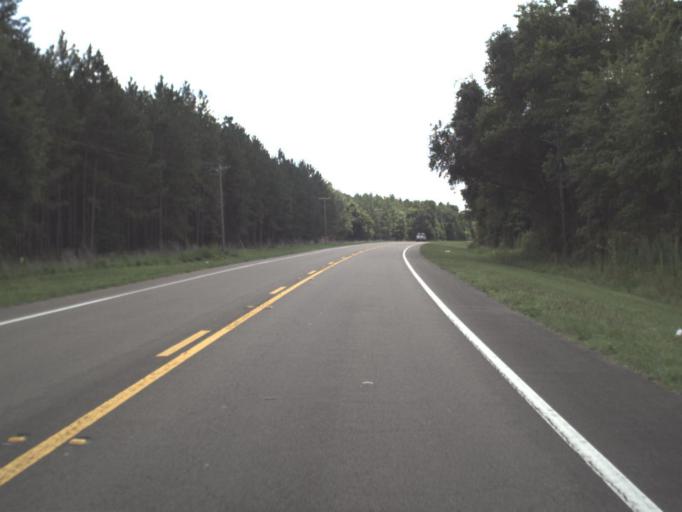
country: US
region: Florida
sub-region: Alachua County
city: Alachua
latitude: 29.8265
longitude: -82.3920
